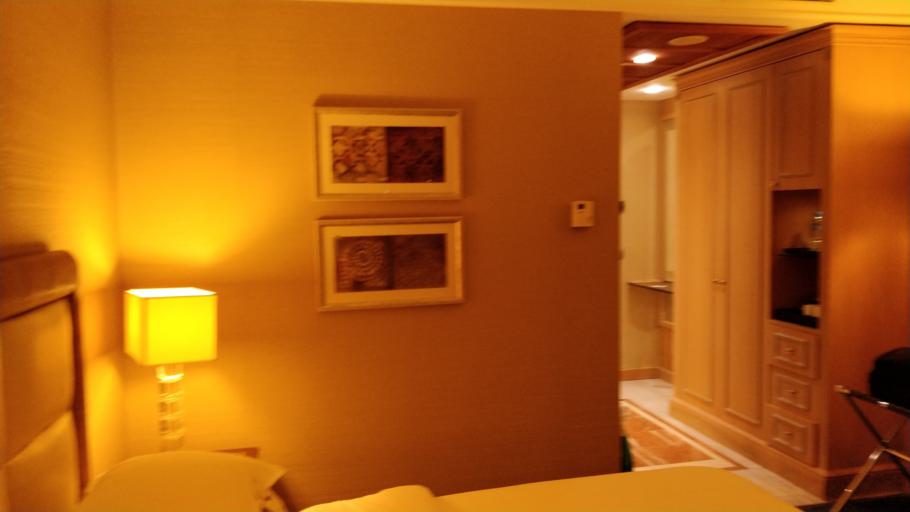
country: DZ
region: Tipaza
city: Zeralda
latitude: 36.7624
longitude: 2.8730
